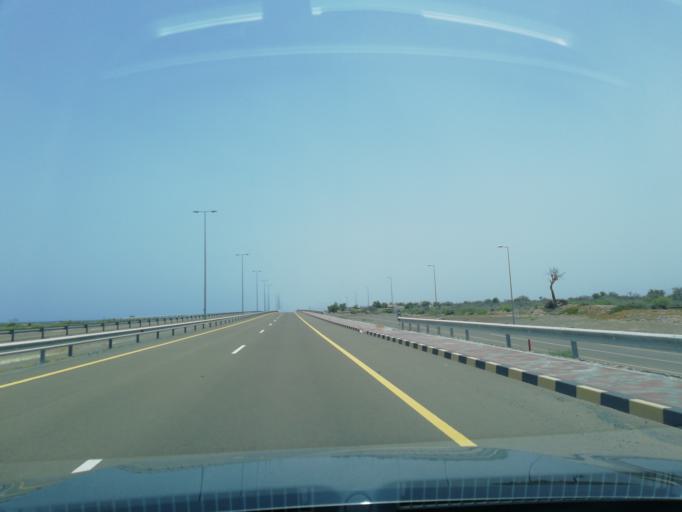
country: OM
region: Al Batinah
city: Shinas
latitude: 24.9000
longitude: 56.3967
